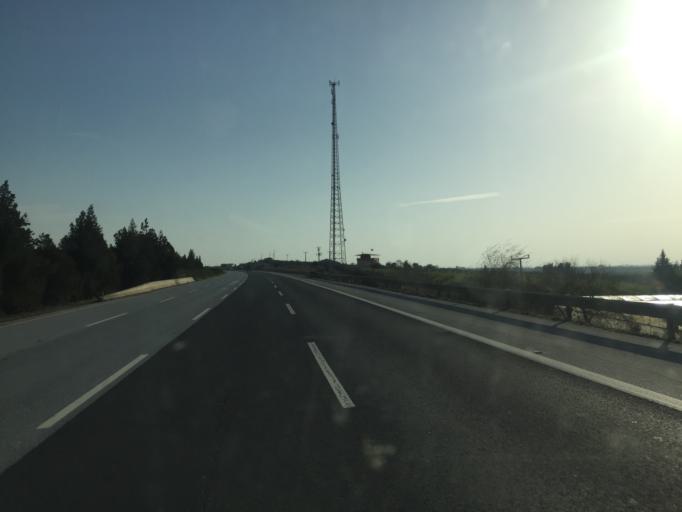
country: TR
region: Mersin
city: Yenice
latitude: 37.0225
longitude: 35.0841
